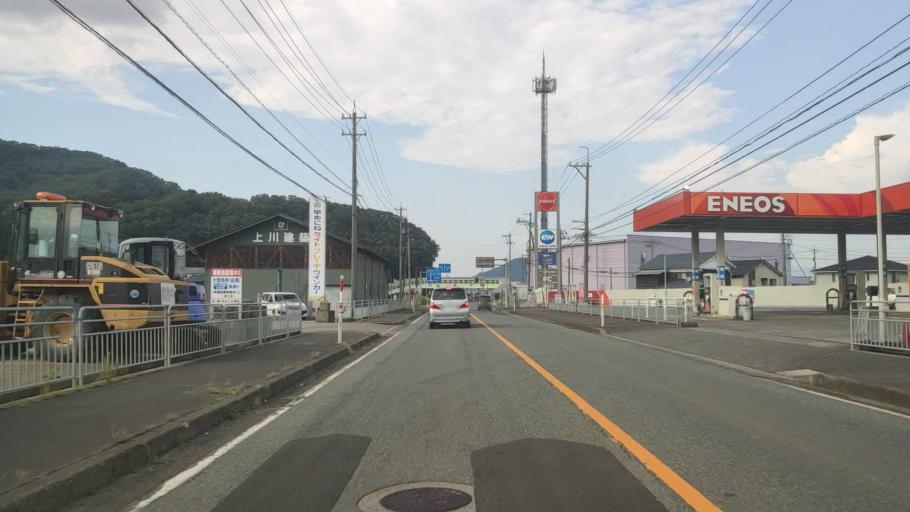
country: JP
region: Fukui
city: Takefu
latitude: 35.8709
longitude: 136.1550
